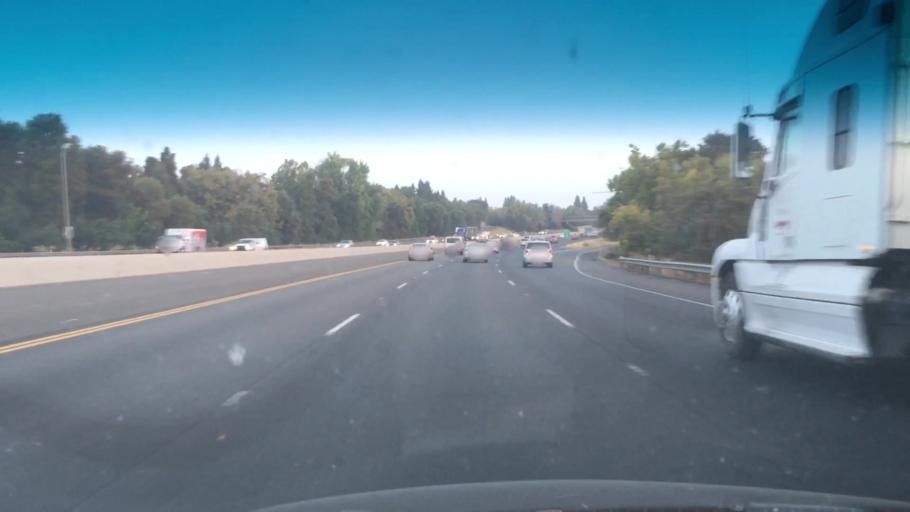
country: US
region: California
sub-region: Sacramento County
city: Parkway
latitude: 38.4778
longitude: -121.5071
